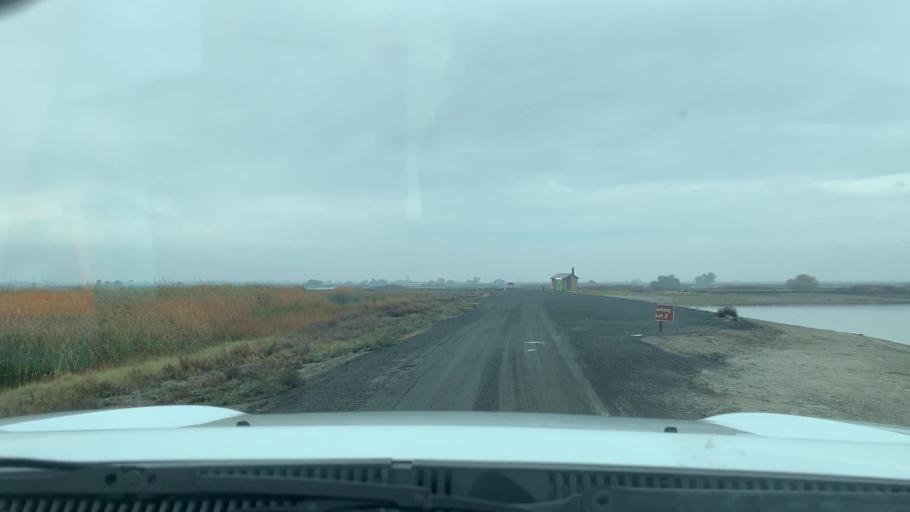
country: US
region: California
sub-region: Kern County
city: Lost Hills
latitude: 35.7336
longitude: -119.6078
